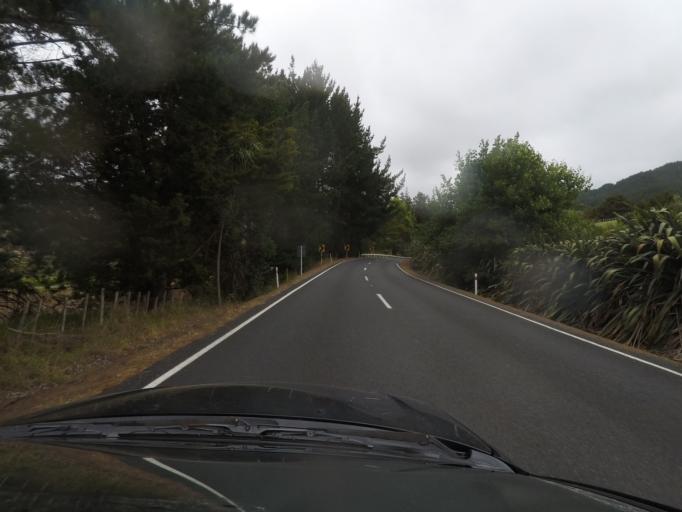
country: NZ
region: Auckland
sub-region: Auckland
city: Warkworth
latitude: -36.2674
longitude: 174.7007
